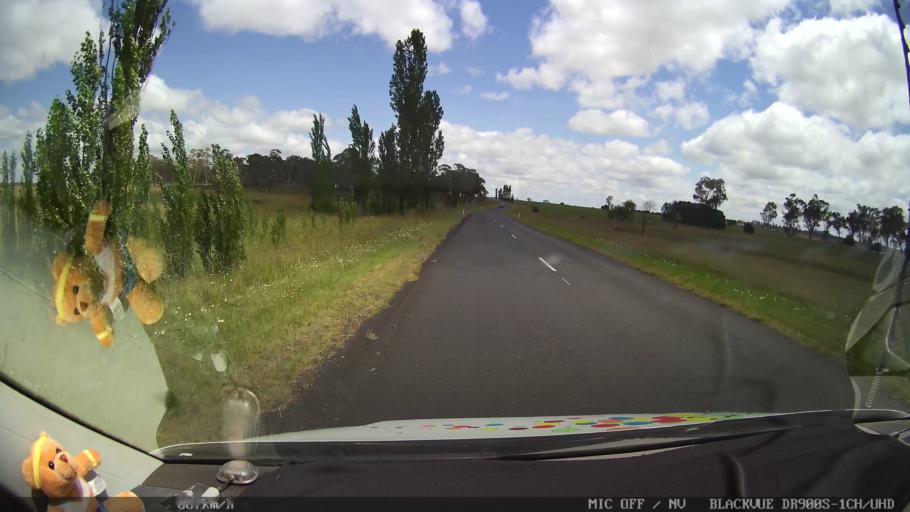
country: AU
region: New South Wales
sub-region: Glen Innes Severn
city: Glen Innes
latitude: -29.6680
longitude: 151.6942
